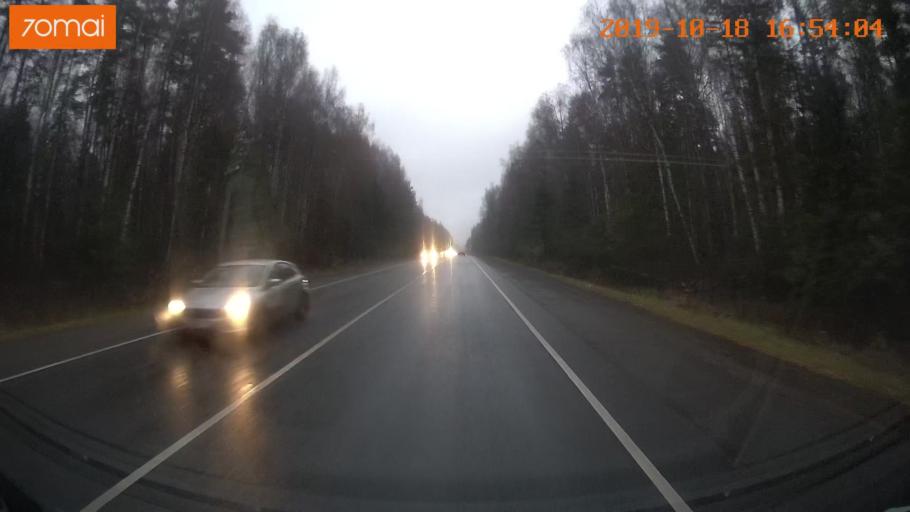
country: RU
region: Ivanovo
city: Nerl'
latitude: 56.6243
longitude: 40.5665
